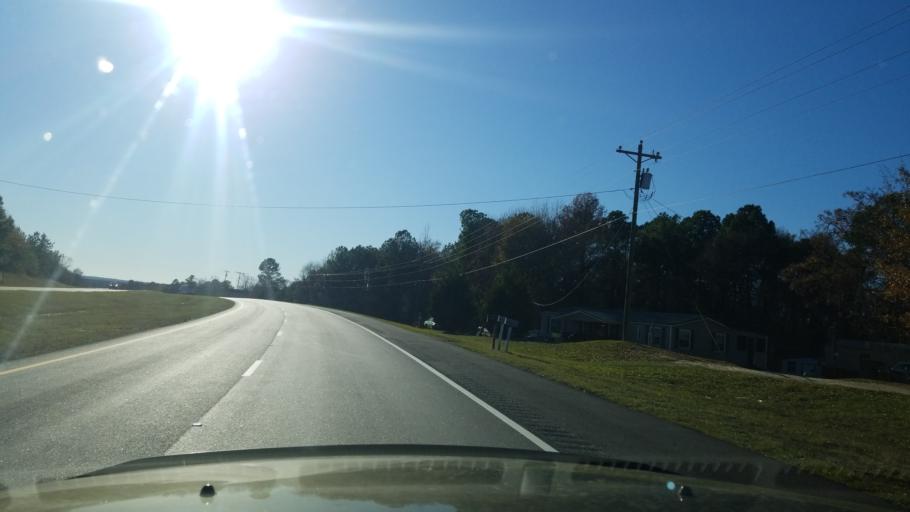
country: US
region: Georgia
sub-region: Talbot County
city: Talbotton
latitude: 32.5742
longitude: -84.5963
